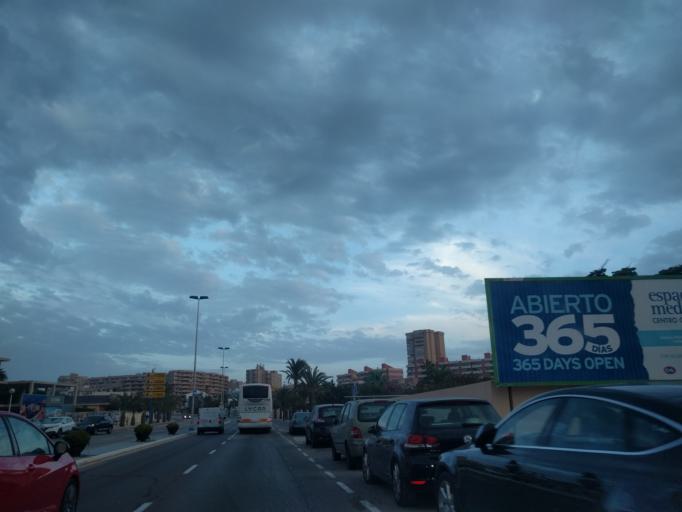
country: ES
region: Murcia
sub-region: Murcia
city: La Manga del Mar Menor
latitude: 37.6690
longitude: -0.7292
